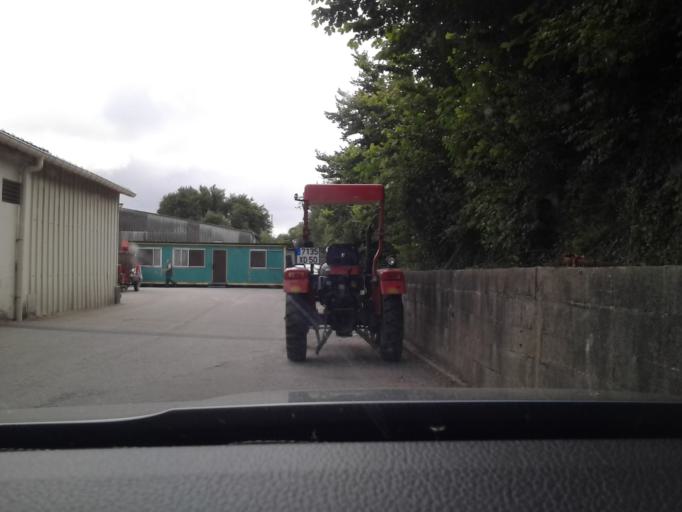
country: FR
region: Lower Normandy
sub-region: Departement de la Manche
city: Valognes
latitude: 49.5032
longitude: -1.4589
